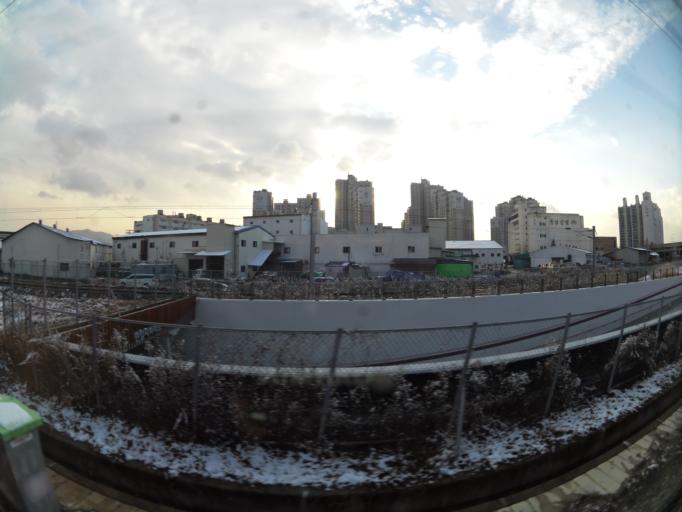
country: KR
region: Daejeon
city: Daejeon
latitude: 36.3423
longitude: 127.4279
